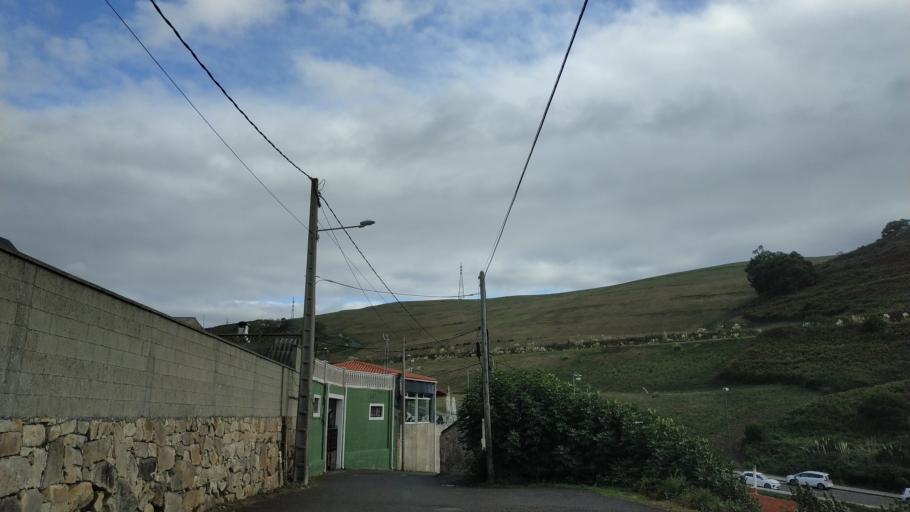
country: ES
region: Galicia
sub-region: Provincia da Coruna
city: A Coruna
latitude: 43.3727
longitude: -8.4457
